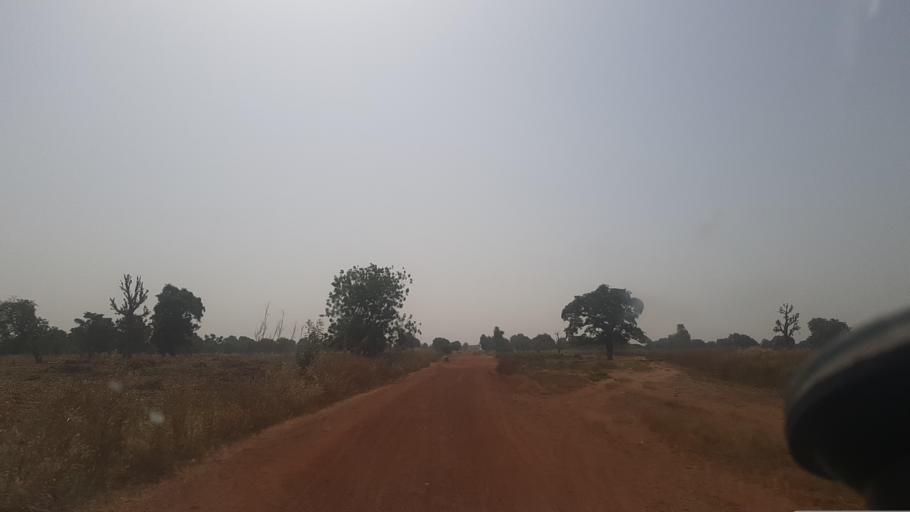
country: ML
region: Segou
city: Baroueli
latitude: 13.0085
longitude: -6.4212
